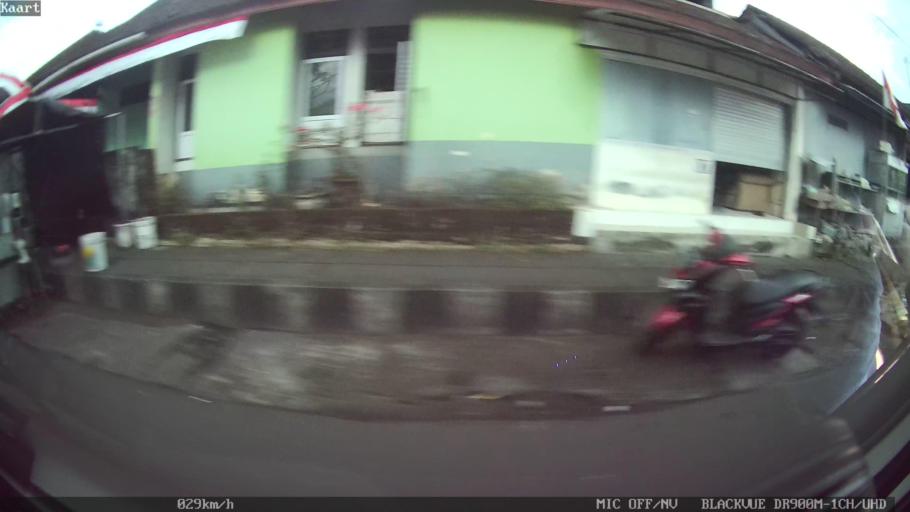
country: ID
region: Bali
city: Tabanan
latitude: -8.5404
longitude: 115.1250
